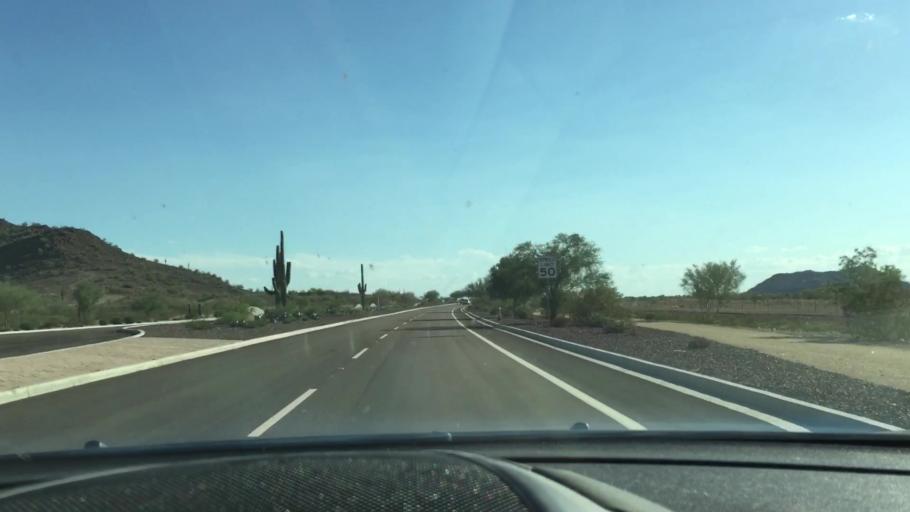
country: US
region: Arizona
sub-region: Maricopa County
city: Sun City West
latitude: 33.7532
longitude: -112.2543
